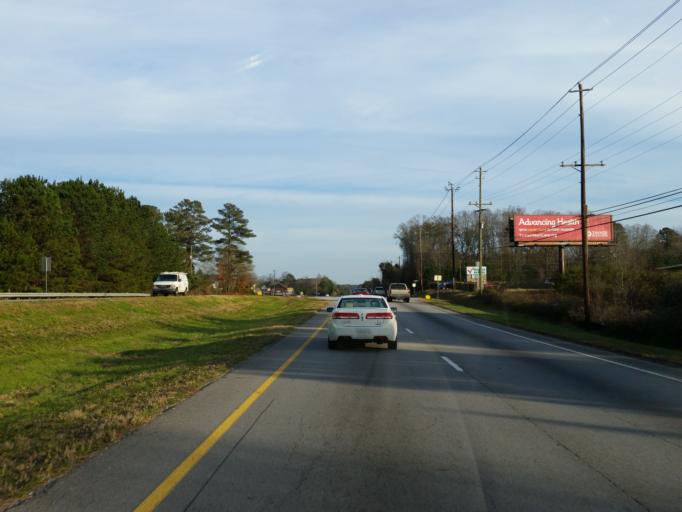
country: US
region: Georgia
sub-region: Paulding County
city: Hiram
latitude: 33.8824
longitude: -84.7268
